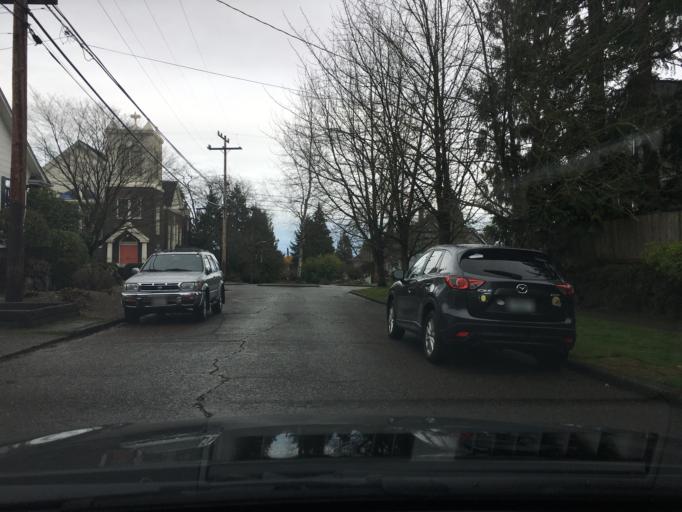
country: US
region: Washington
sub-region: King County
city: Seattle
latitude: 47.6626
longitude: -122.3308
